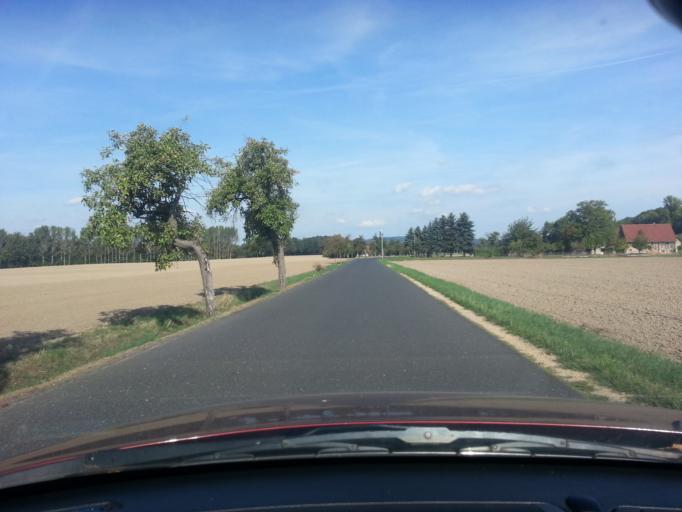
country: DE
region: Saxony
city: Reichenbach
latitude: 51.1072
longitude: 14.8319
